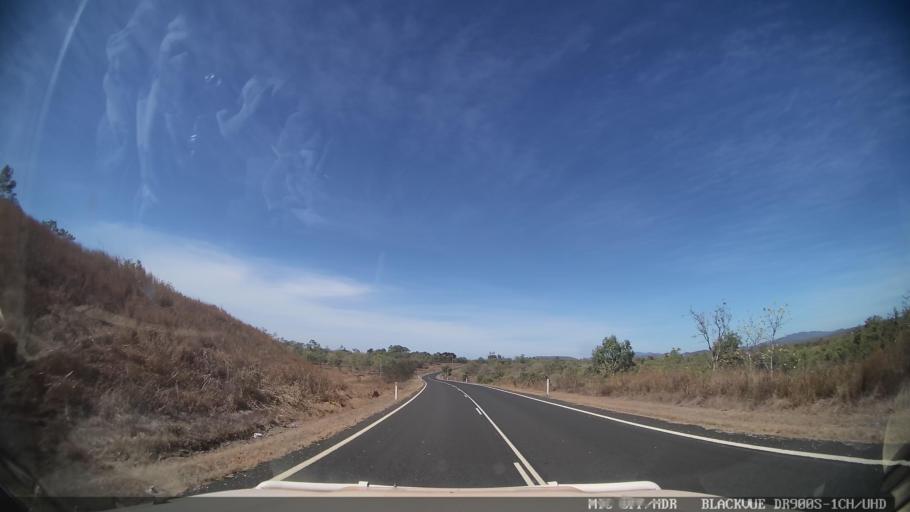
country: AU
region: Queensland
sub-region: Cook
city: Cooktown
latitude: -15.8656
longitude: 144.8170
